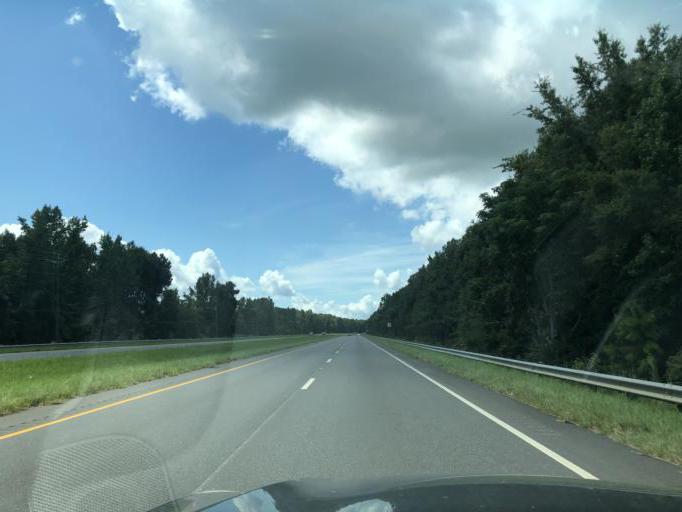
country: US
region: Alabama
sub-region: Barbour County
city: Eufaula
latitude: 31.9753
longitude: -85.1150
